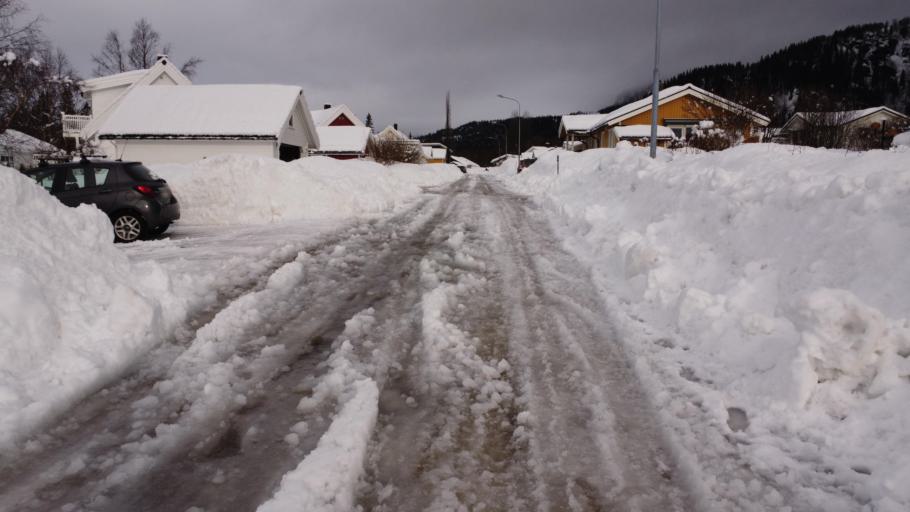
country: NO
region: Nordland
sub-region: Rana
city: Mo i Rana
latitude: 66.3331
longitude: 14.1520
